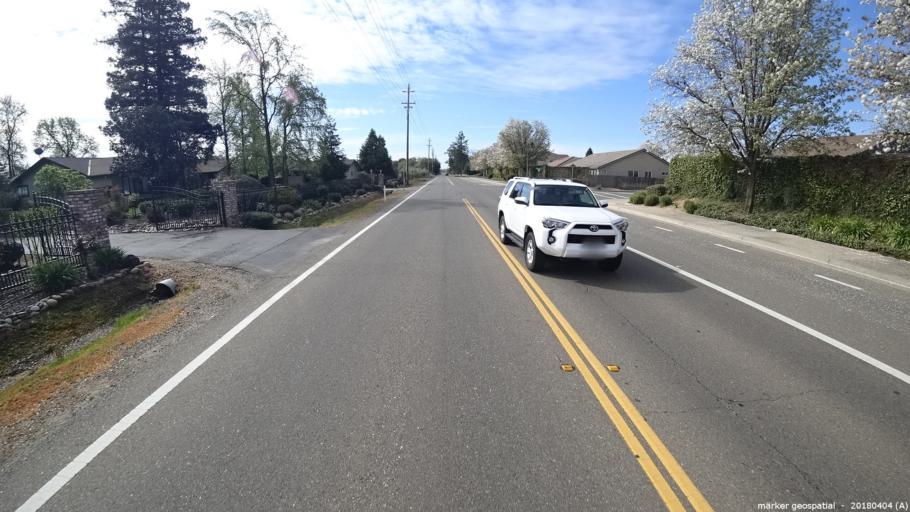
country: US
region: California
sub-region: Sacramento County
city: Galt
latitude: 38.2682
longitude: -121.2826
